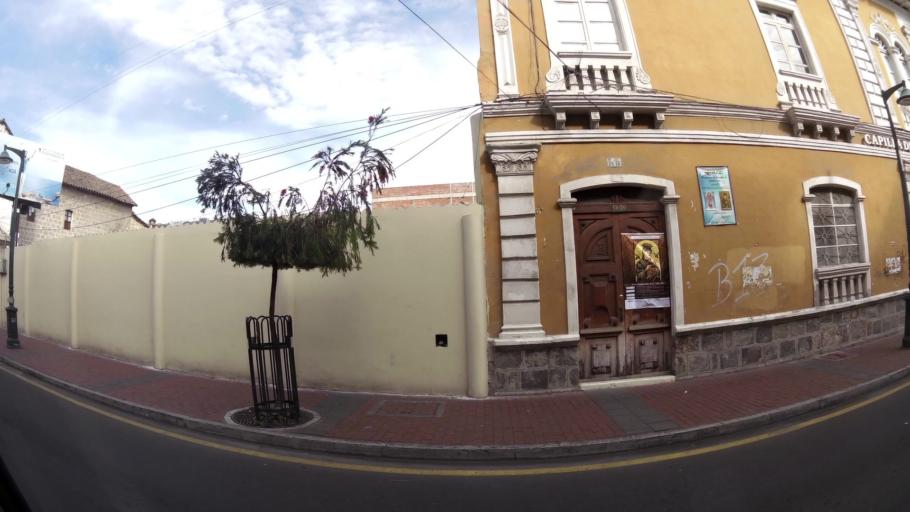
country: EC
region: Tungurahua
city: Ambato
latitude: -1.2424
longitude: -78.6266
